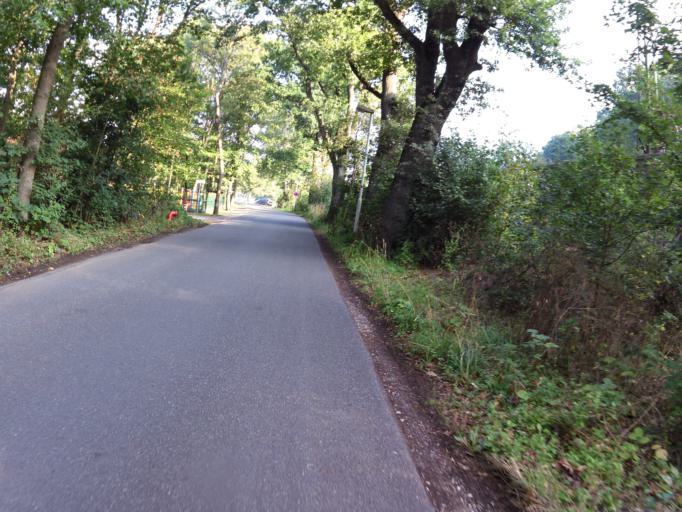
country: DE
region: Lower Saxony
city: Verden
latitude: 52.9447
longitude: 9.2308
